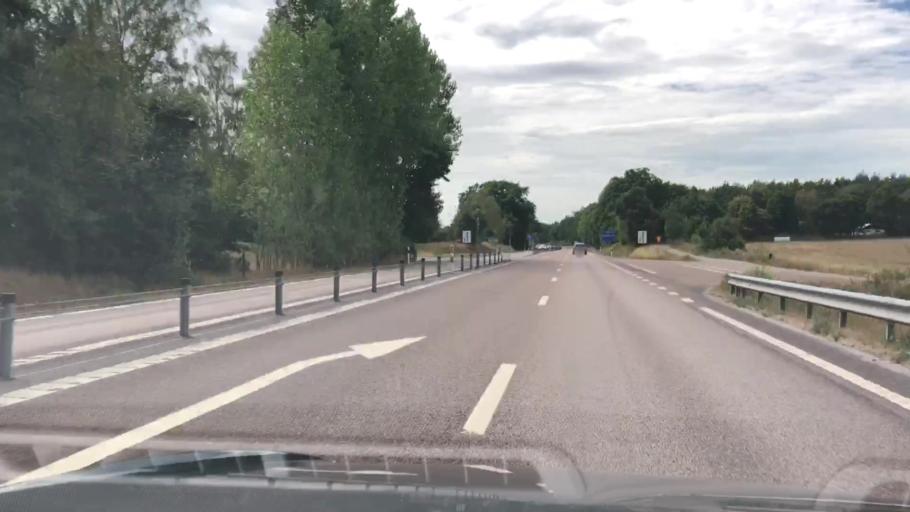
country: SE
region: Kalmar
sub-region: Torsas Kommun
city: Torsas
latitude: 56.3166
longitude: 16.0229
